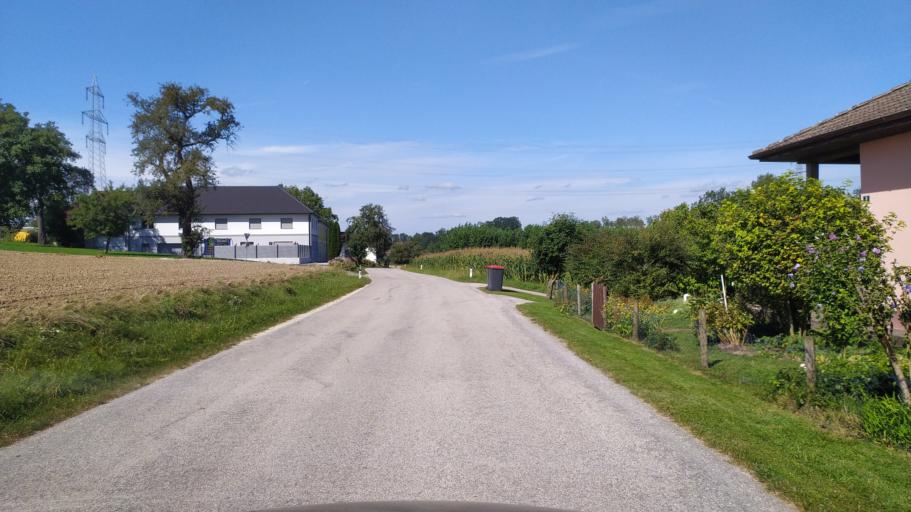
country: AT
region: Lower Austria
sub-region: Politischer Bezirk Amstetten
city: Strengberg
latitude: 48.1313
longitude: 14.6731
